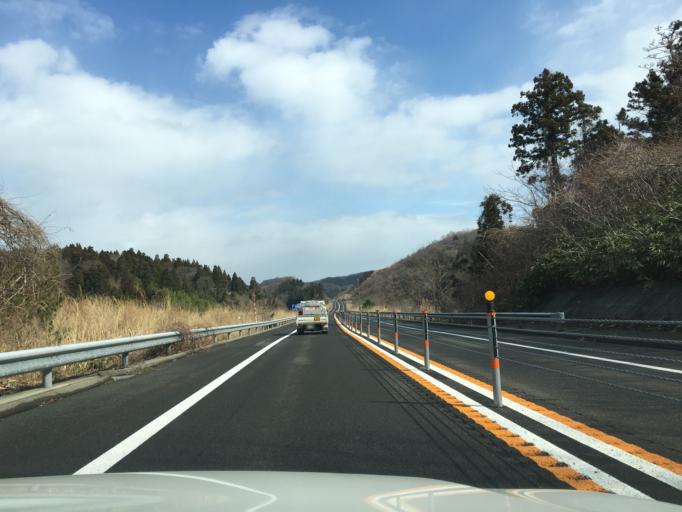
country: JP
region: Akita
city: Akita Shi
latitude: 39.4843
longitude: 140.0536
